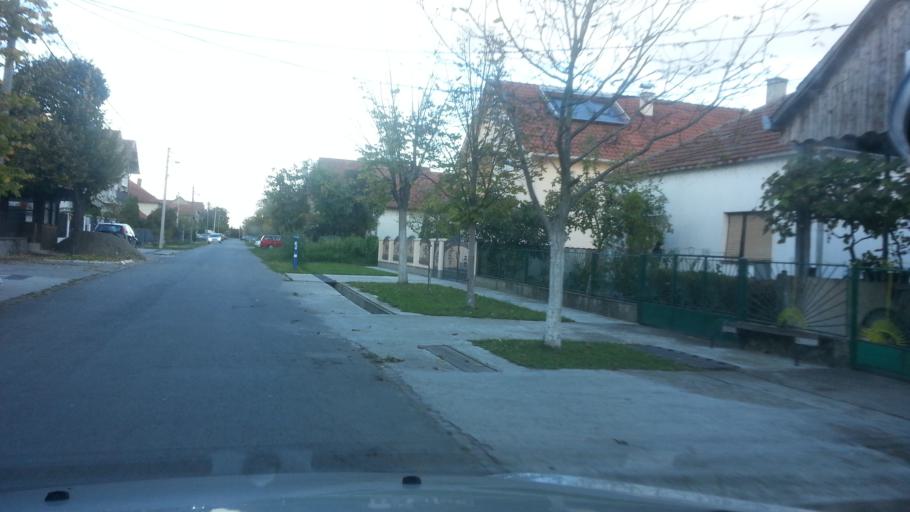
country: RS
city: Novi Banovci
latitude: 44.9035
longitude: 20.2668
